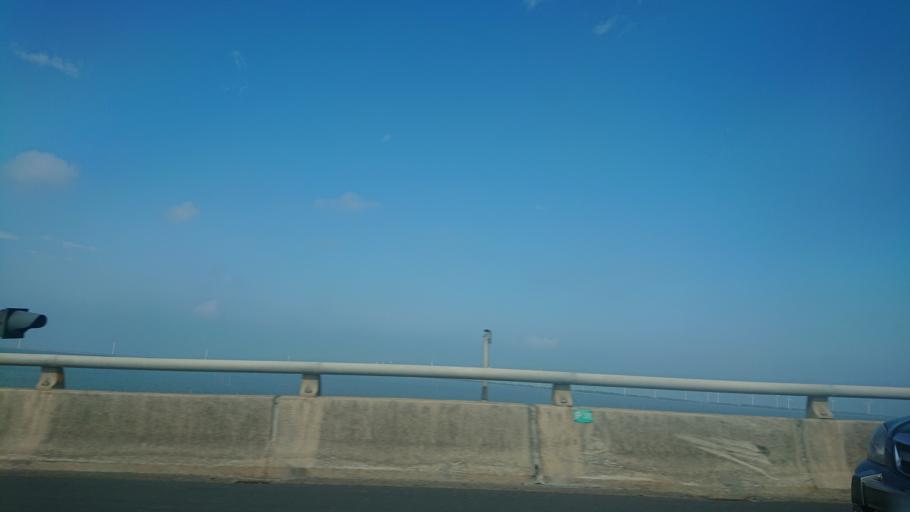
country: TW
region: Taiwan
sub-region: Changhua
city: Chang-hua
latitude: 24.0852
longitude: 120.4242
